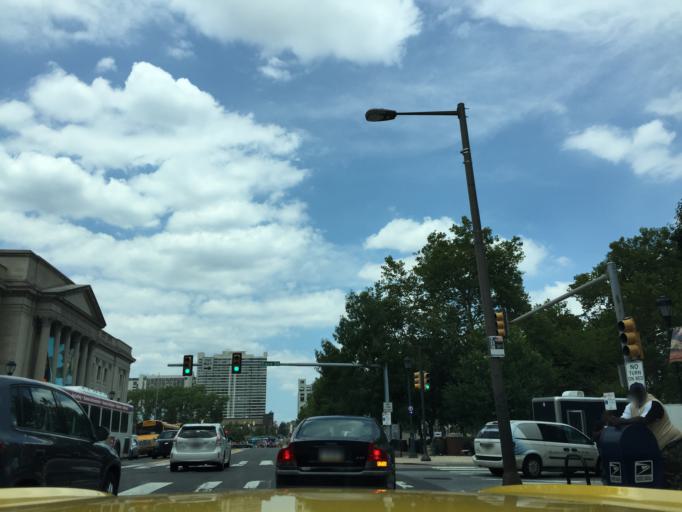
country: US
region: Pennsylvania
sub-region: Philadelphia County
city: Philadelphia
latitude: 39.9573
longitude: -75.1724
